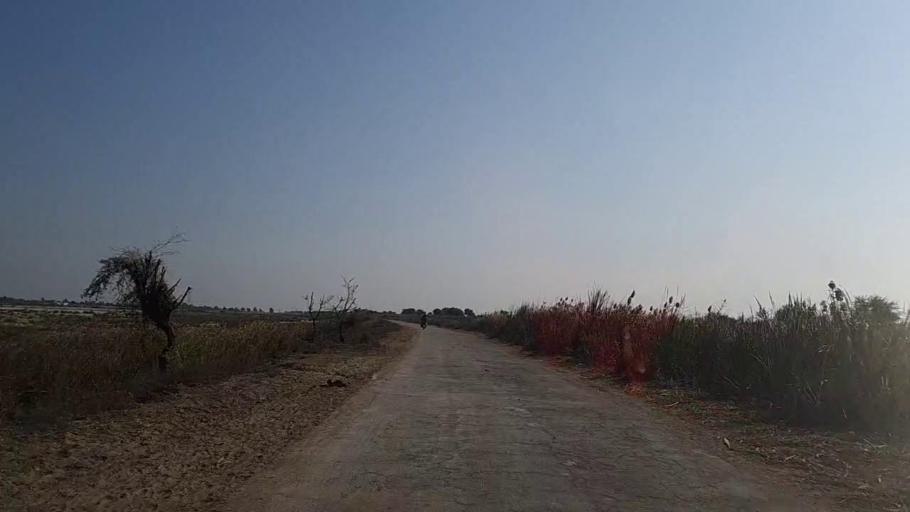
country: PK
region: Sindh
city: Sanghar
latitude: 25.9816
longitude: 69.0235
